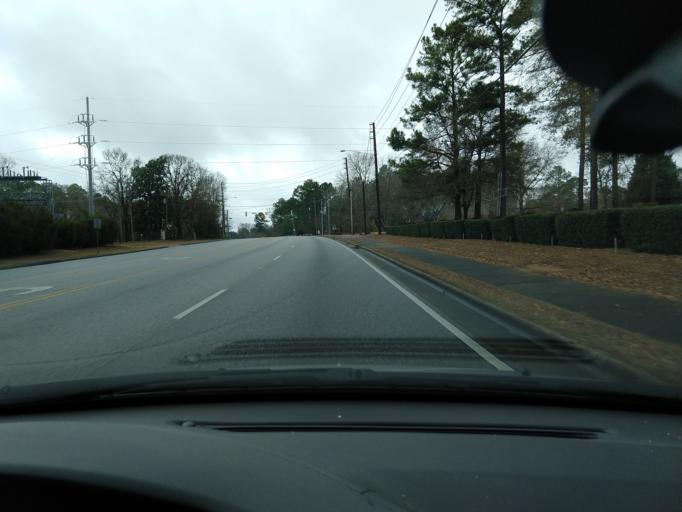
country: US
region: Alabama
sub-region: Houston County
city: Dothan
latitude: 31.2482
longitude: -85.4369
